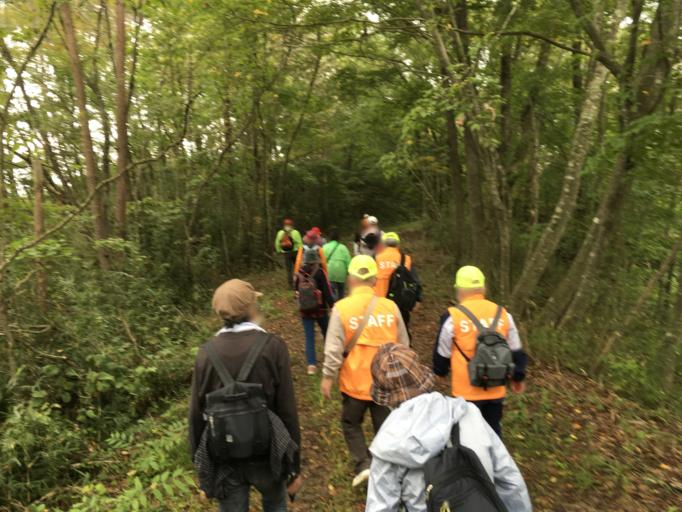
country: JP
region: Iwate
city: Ichinoseki
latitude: 38.8818
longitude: 141.0816
